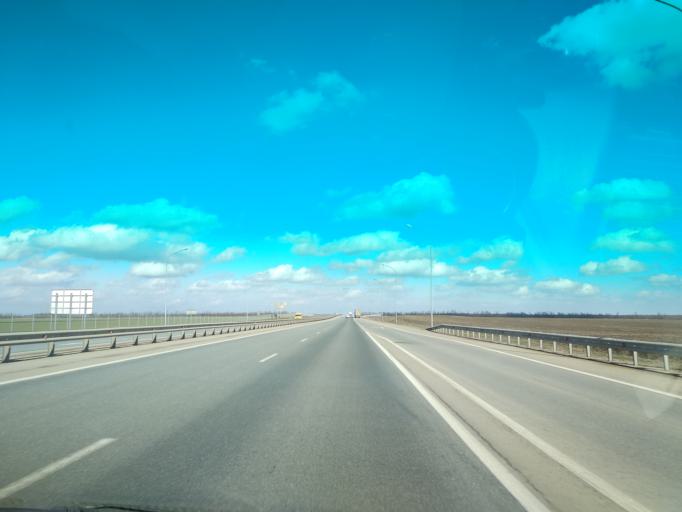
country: RU
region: Krasnodarskiy
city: Korenovsk
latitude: 45.5877
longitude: 39.5164
